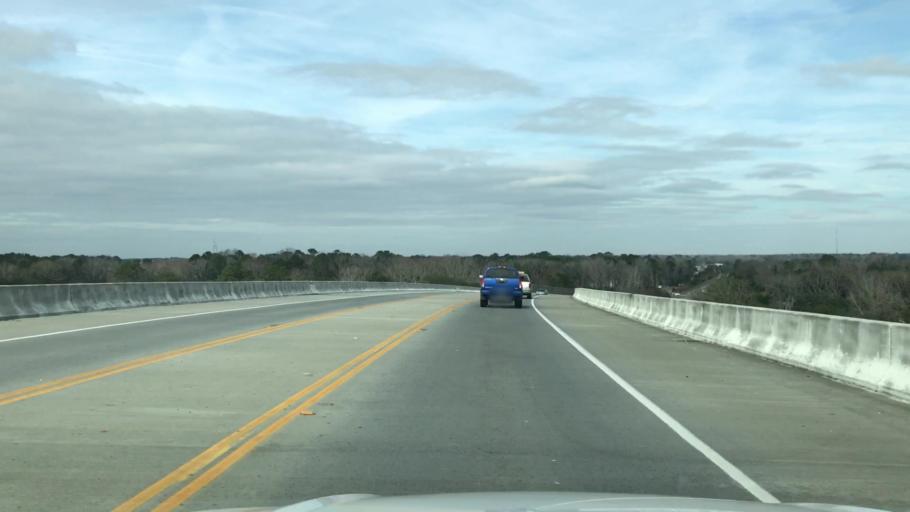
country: US
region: South Carolina
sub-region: Charleston County
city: Shell Point
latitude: 32.7861
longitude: -80.1076
